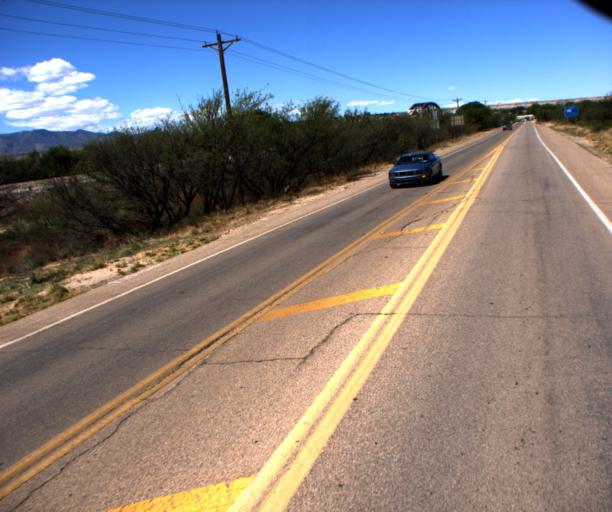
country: US
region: Arizona
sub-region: Cochise County
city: Benson
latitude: 31.9650
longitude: -110.2754
